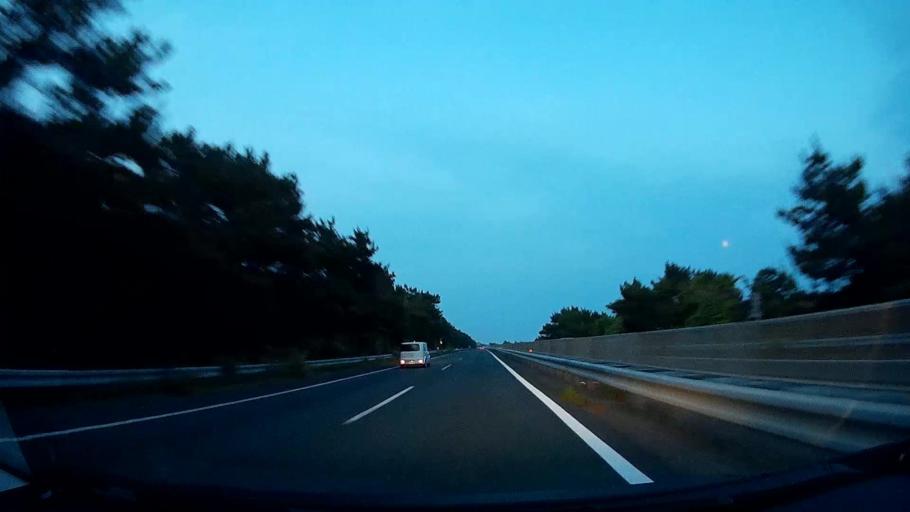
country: JP
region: Shizuoka
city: Kosai-shi
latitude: 34.6780
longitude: 137.6166
